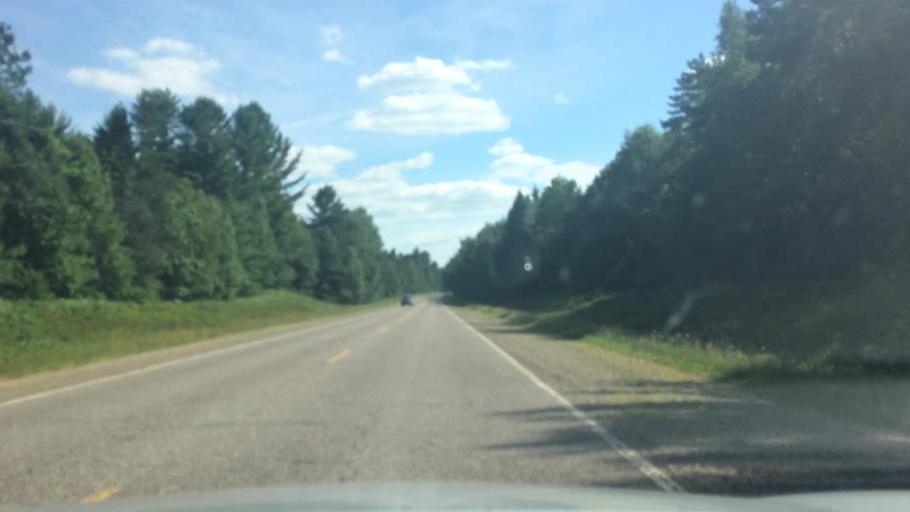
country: US
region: Wisconsin
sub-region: Vilas County
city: Lac du Flambeau
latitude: 46.0686
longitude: -89.6446
